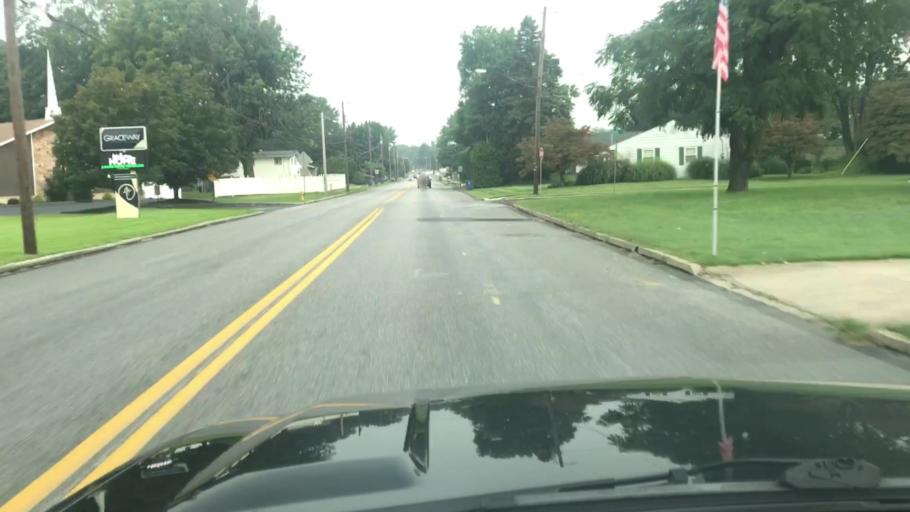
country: US
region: Pennsylvania
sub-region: Cumberland County
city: Shiremanstown
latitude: 40.2336
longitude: -76.9567
